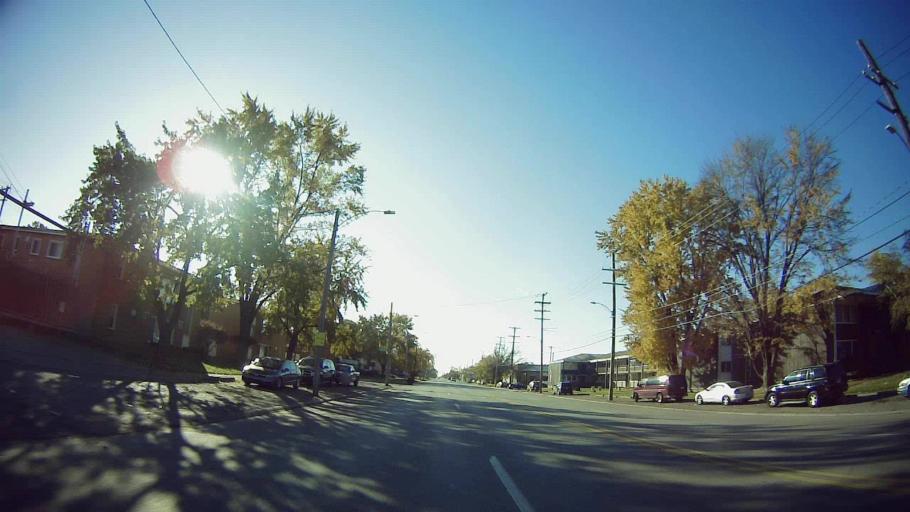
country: US
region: Michigan
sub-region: Oakland County
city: Oak Park
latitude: 42.4116
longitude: -83.1991
